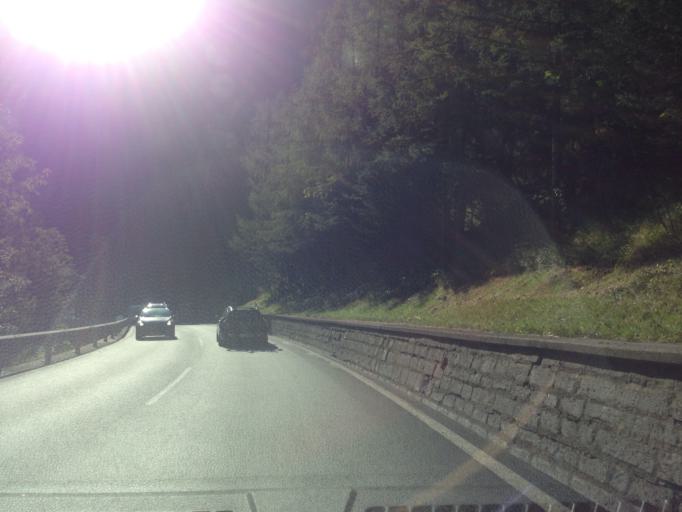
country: AT
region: Tyrol
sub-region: Politischer Bezirk Imst
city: Nassereith
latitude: 47.3567
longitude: 10.8517
